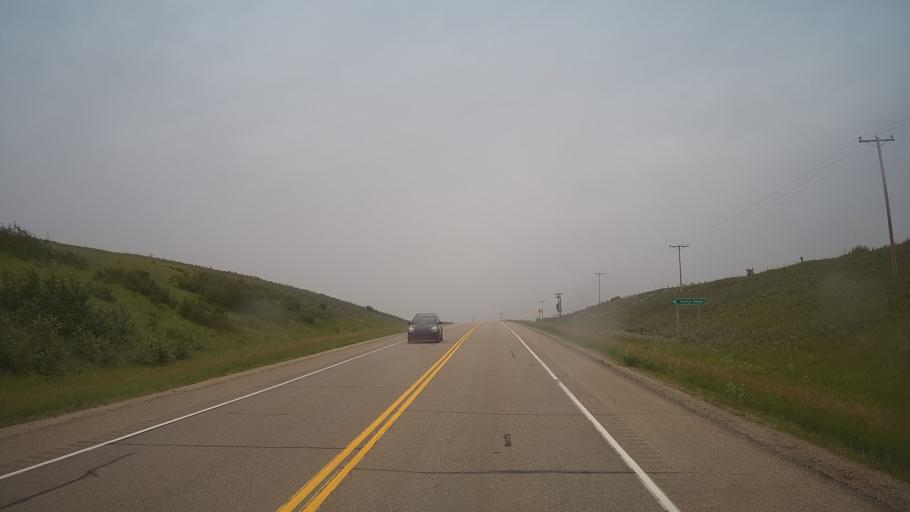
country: CA
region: Saskatchewan
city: Biggar
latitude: 52.0577
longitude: -107.8827
